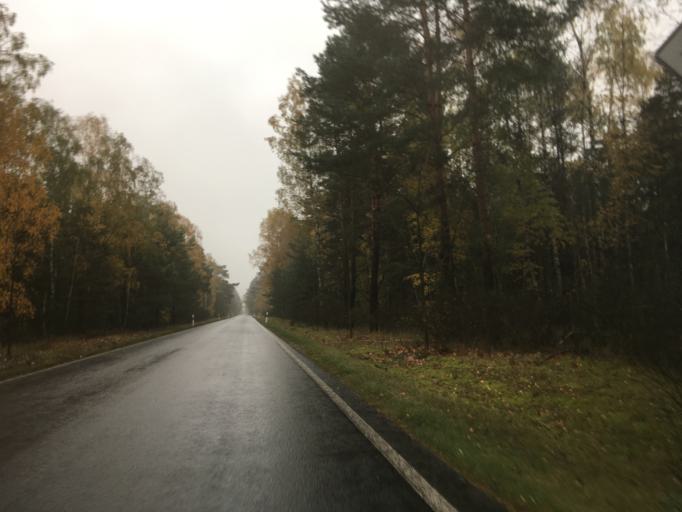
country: DE
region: Brandenburg
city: Halbe
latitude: 52.0324
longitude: 13.7683
